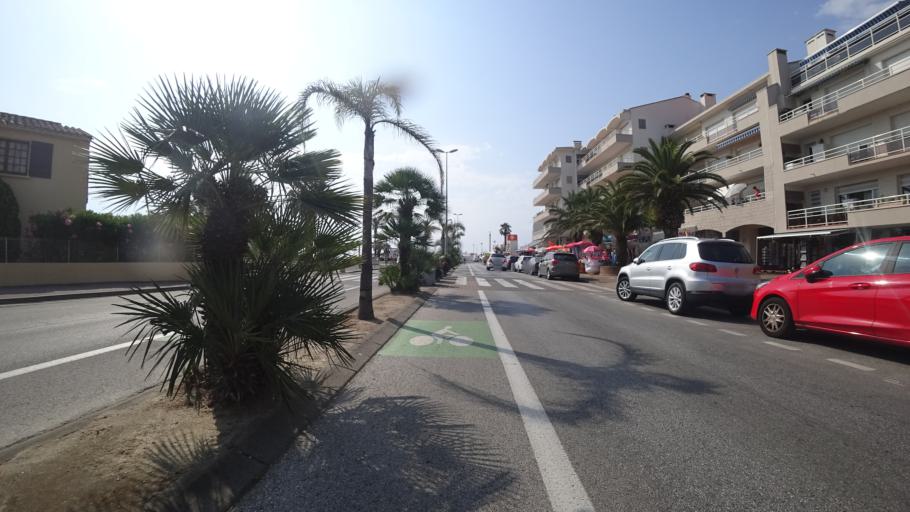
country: FR
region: Languedoc-Roussillon
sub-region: Departement des Pyrenees-Orientales
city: Saint-Cyprien-Plage
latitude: 42.6239
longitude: 3.0359
